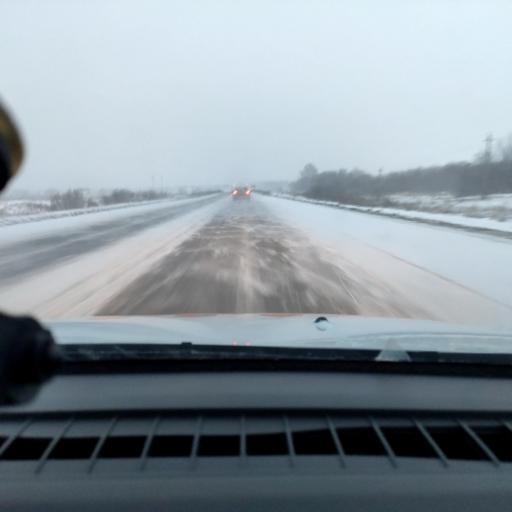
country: RU
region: Samara
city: Kinel'-Cherkassy
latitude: 53.4187
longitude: 51.4698
